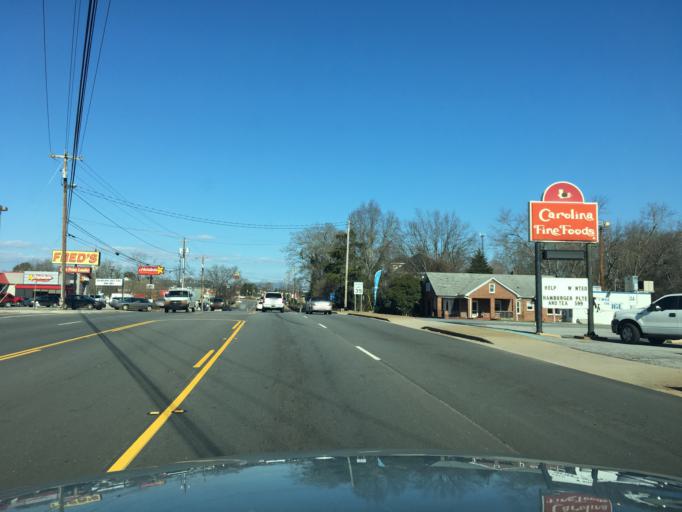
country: US
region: South Carolina
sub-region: Pickens County
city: Pickens
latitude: 34.8805
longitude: -82.7022
